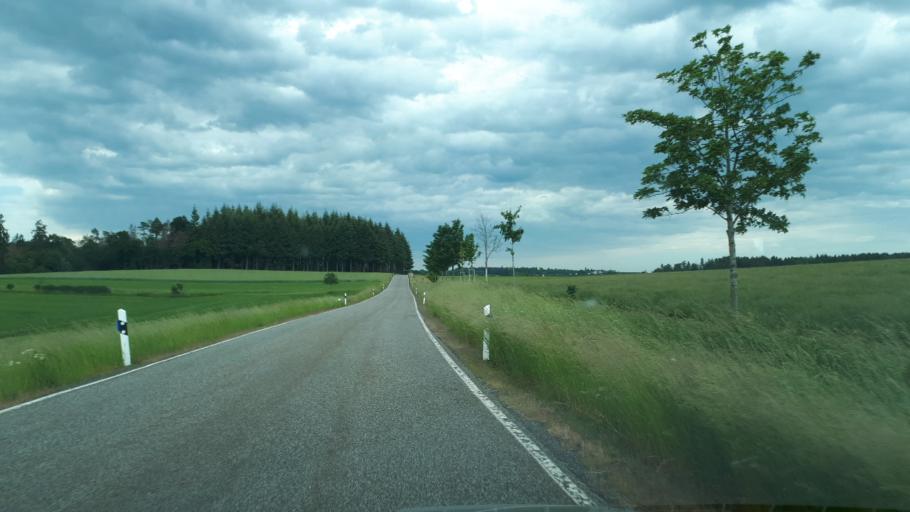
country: DE
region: Rheinland-Pfalz
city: Filz
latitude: 50.1745
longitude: 6.9851
